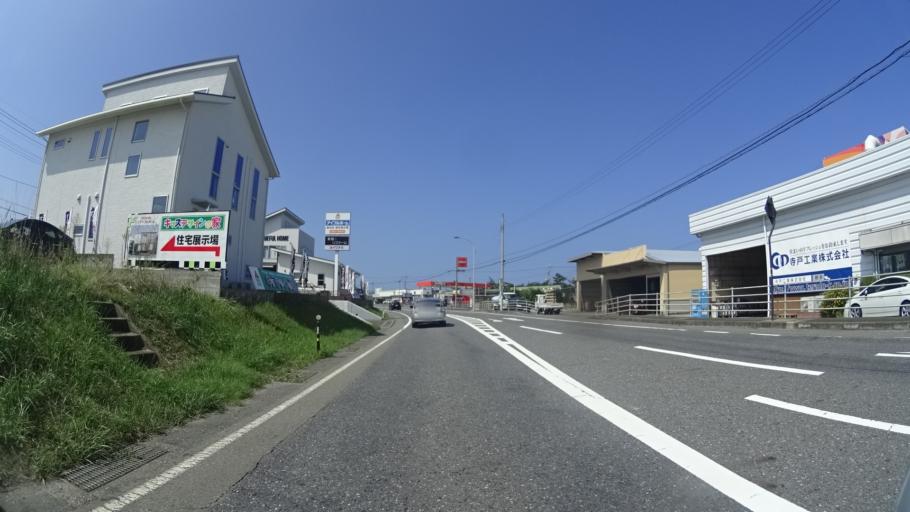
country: JP
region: Shimane
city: Masuda
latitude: 34.6902
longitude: 131.8109
